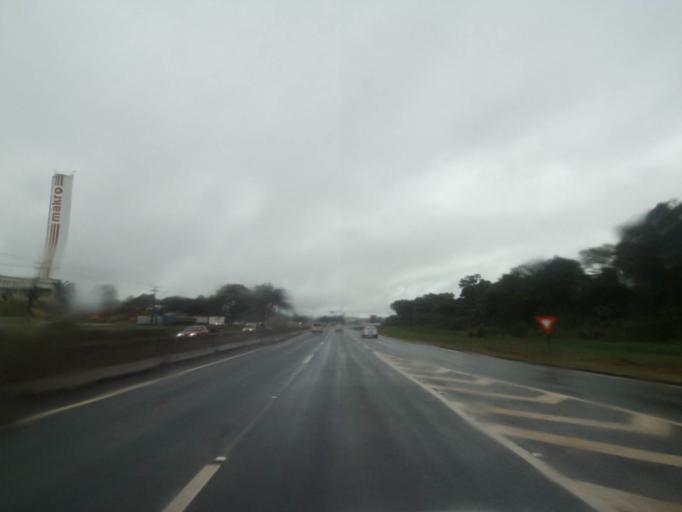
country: PY
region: Alto Parana
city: Ciudad del Este
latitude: -25.5097
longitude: -54.5746
